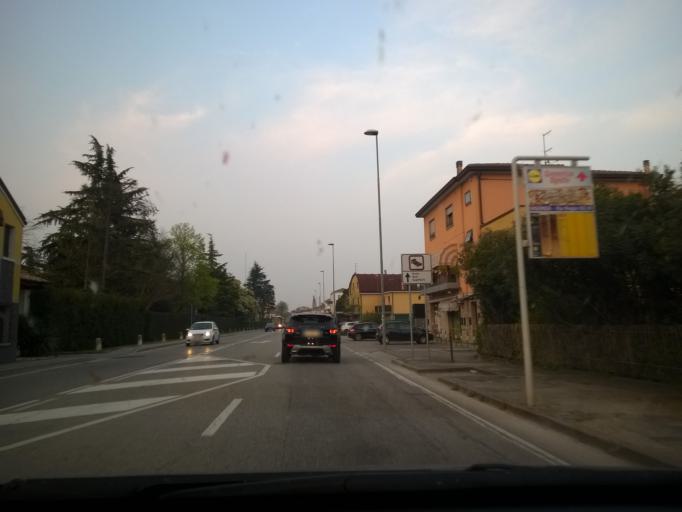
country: IT
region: Veneto
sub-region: Provincia di Padova
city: Noventa
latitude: 45.4221
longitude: 11.9386
